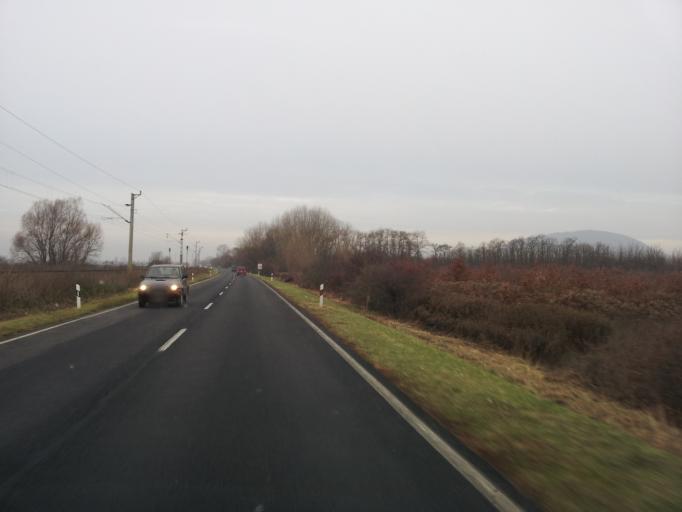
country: HU
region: Veszprem
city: Devecser
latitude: 47.1196
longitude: 17.4110
